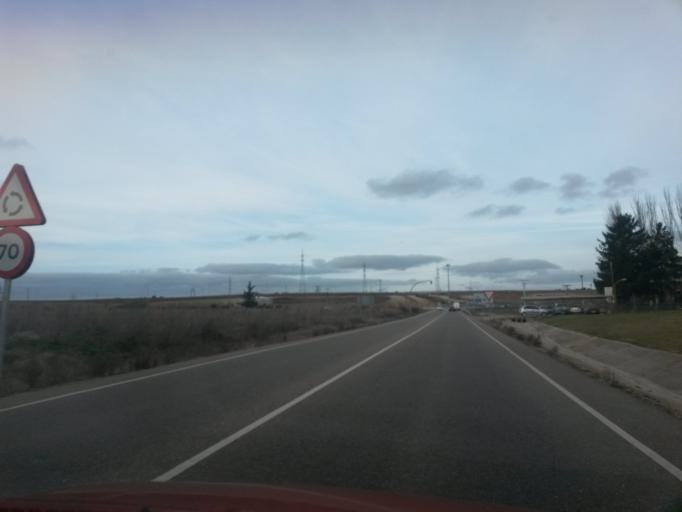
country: ES
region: Castille and Leon
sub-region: Provincia de Salamanca
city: Villares de la Reina
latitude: 40.9956
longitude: -5.6574
